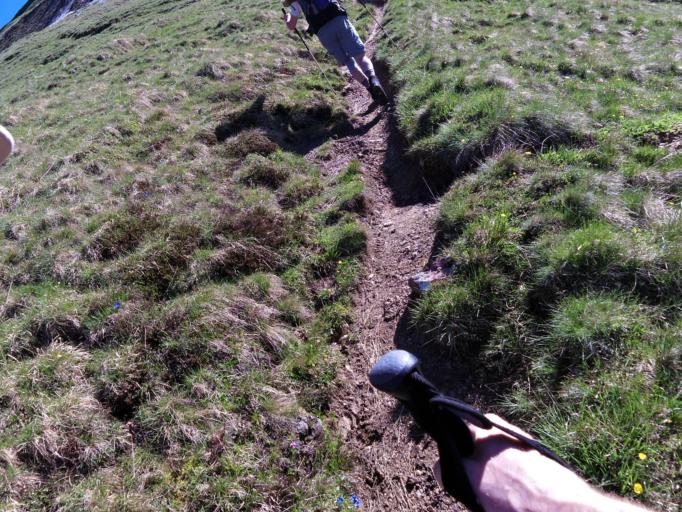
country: AT
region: Tyrol
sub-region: Politischer Bezirk Innsbruck Land
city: Neustift im Stubaital
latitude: 47.1313
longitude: 11.2752
